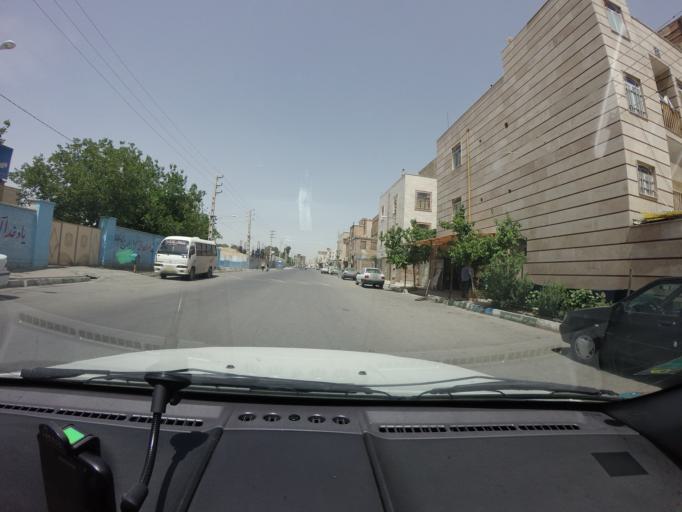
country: IR
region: Tehran
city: Eslamshahr
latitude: 35.5281
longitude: 51.2162
